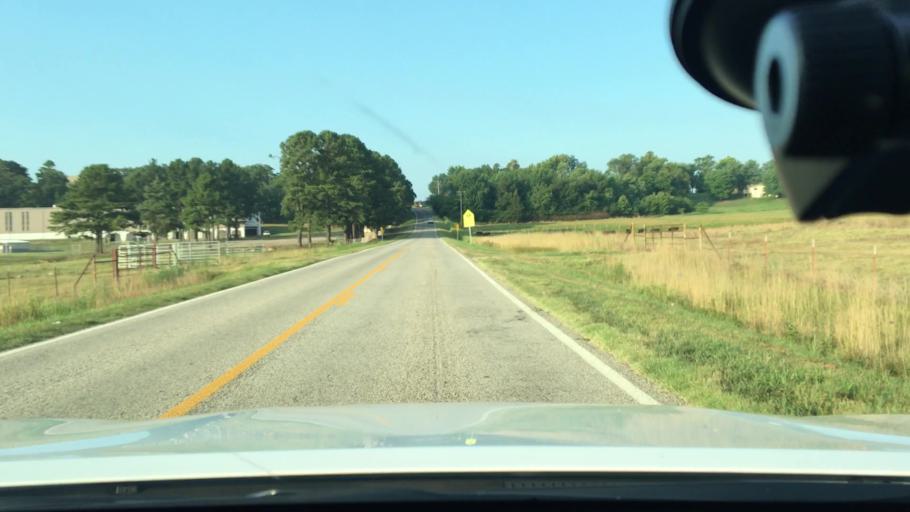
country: US
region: Arkansas
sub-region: Logan County
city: Paris
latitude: 35.3033
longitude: -93.6342
